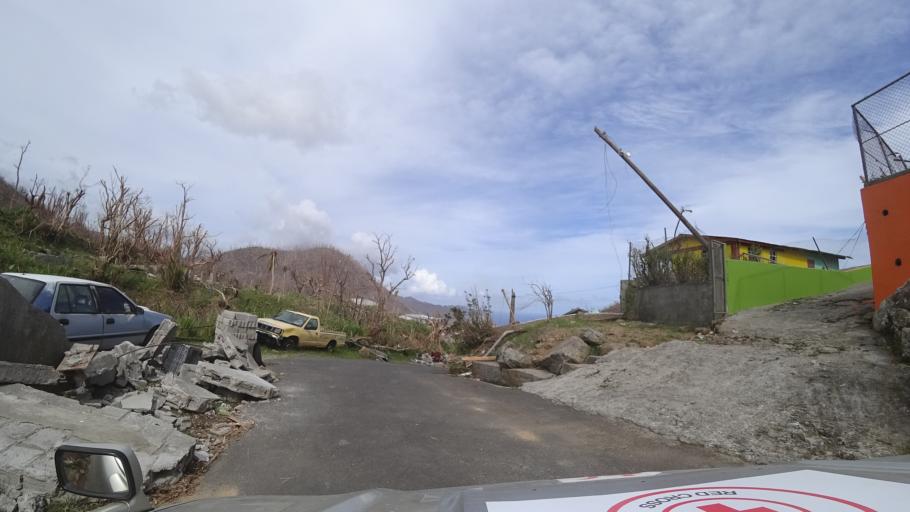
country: DM
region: Saint Patrick
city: Berekua
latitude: 15.2364
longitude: -61.3365
